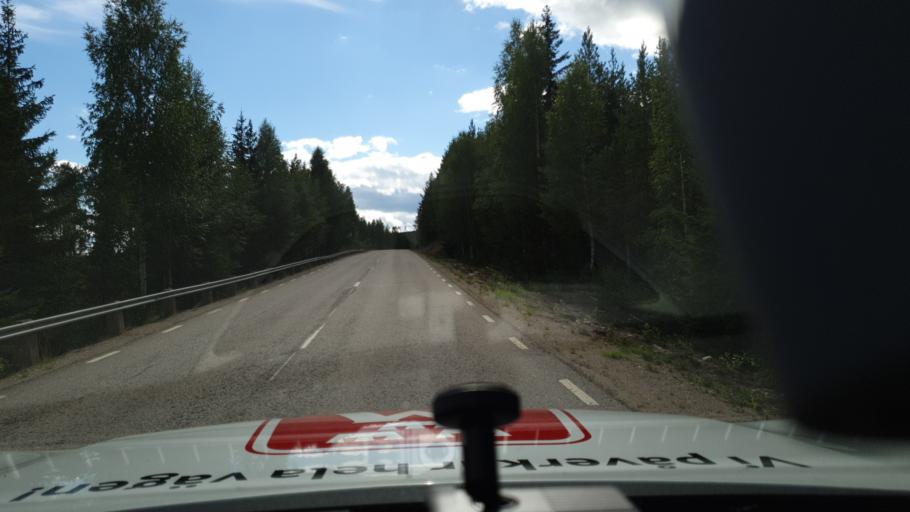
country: NO
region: Hedmark
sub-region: Trysil
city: Innbygda
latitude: 61.0218
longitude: 12.5437
